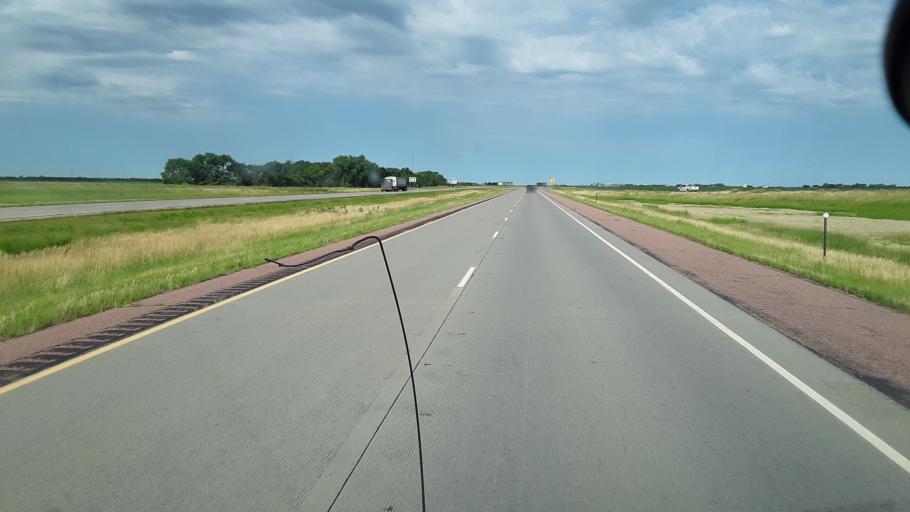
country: US
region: South Dakota
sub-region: Aurora County
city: Plankinton
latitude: 43.6951
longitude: -98.4454
